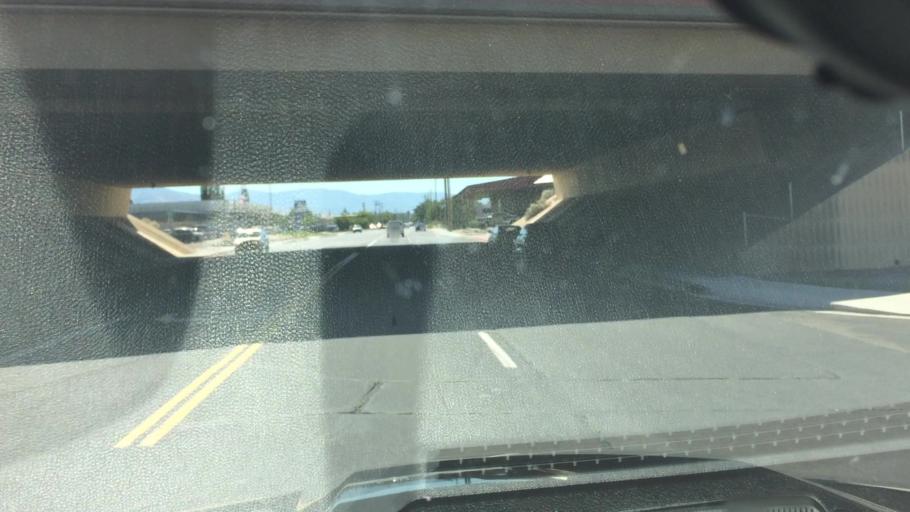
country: US
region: Nevada
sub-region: Washoe County
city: Sparks
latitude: 39.5131
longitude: -119.7807
